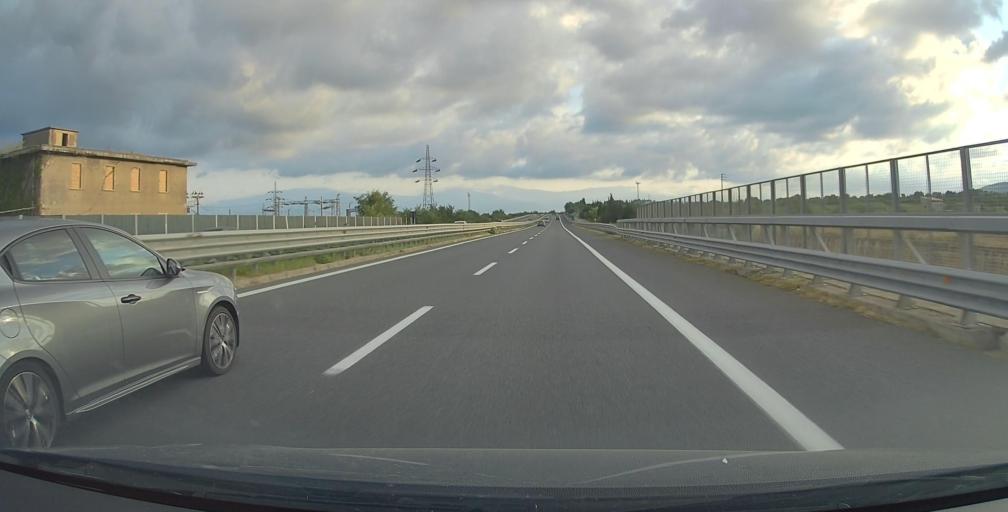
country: IT
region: Calabria
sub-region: Provincia di Catanzaro
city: Acconia
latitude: 38.8094
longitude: 16.2329
